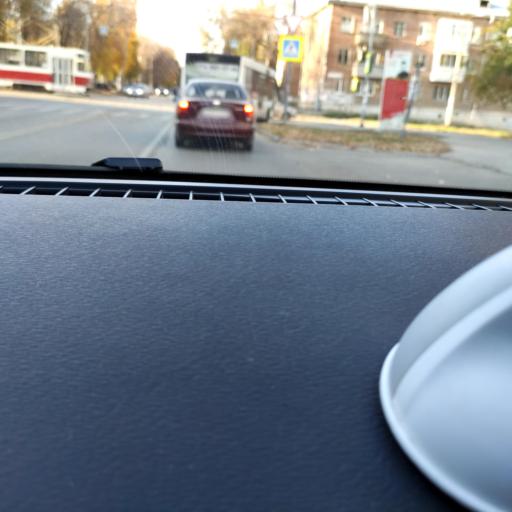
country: RU
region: Samara
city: Samara
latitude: 53.2208
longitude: 50.2309
